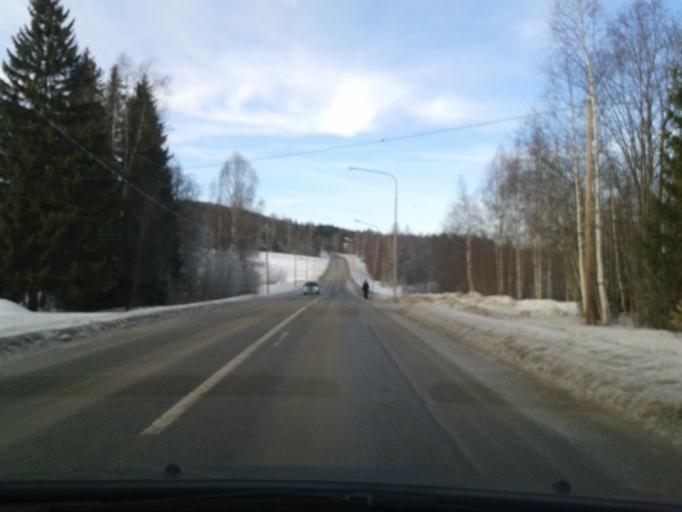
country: SE
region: Vaesternorrland
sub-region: OErnskoeldsviks Kommun
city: Bredbyn
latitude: 63.4857
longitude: 18.0864
